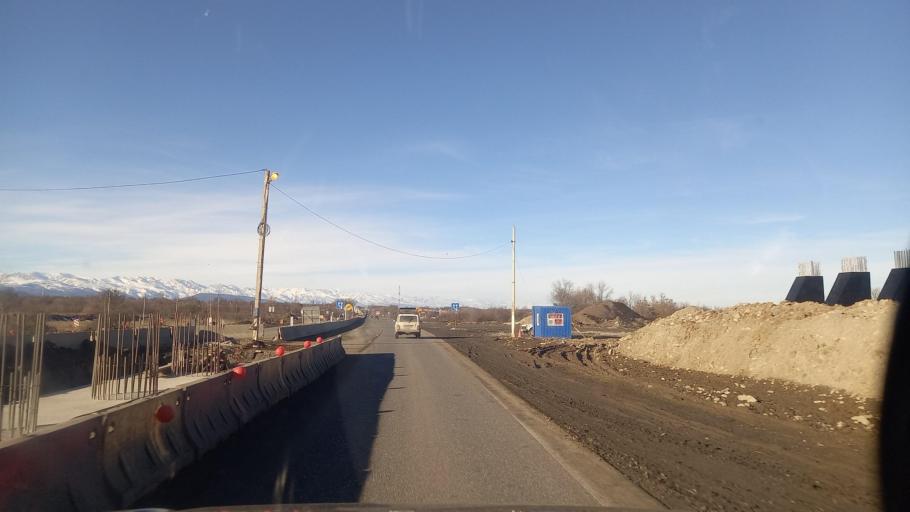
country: RU
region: North Ossetia
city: Gizel'
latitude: 43.0277
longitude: 44.6066
